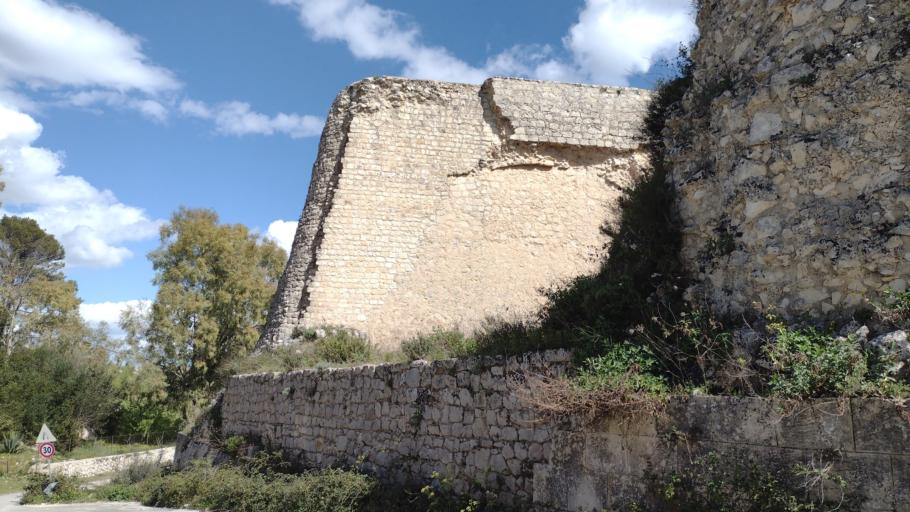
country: IT
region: Sicily
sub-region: Provincia di Siracusa
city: Noto
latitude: 36.9464
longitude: 15.0230
